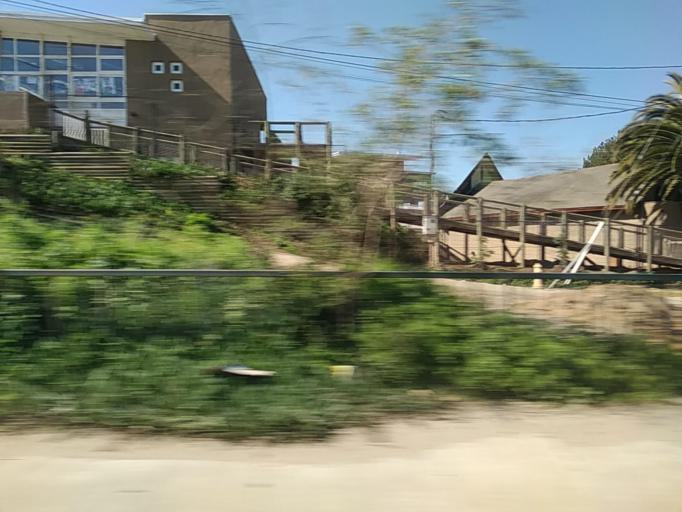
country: CL
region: Valparaiso
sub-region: Provincia de Valparaiso
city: Vina del Mar
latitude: -32.9531
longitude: -71.5389
